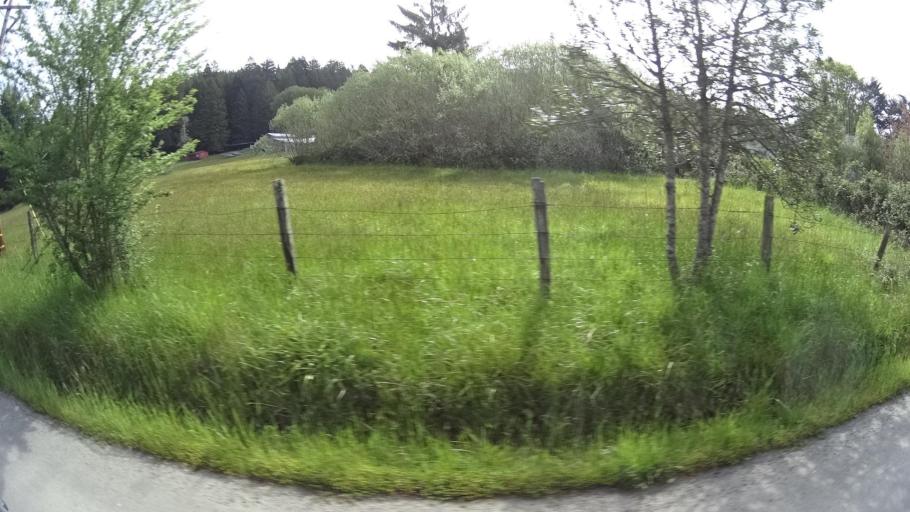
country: US
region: California
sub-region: Humboldt County
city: Myrtletown
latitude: 40.7728
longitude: -124.0738
